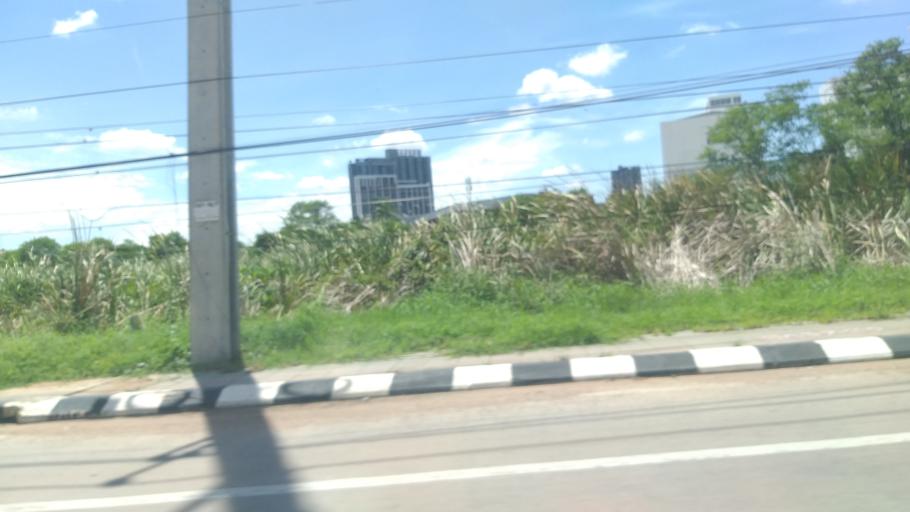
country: TH
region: Khon Kaen
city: Khon Kaen
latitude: 16.4344
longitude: 102.8194
